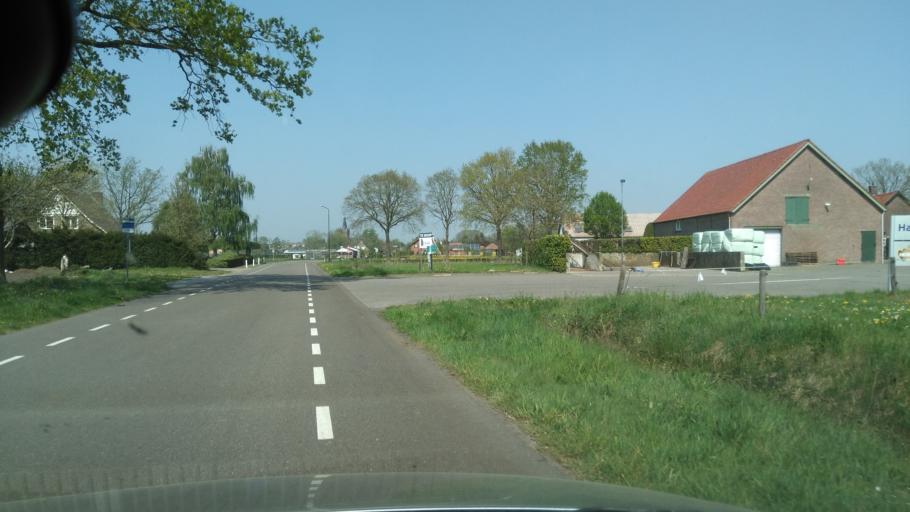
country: NL
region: North Brabant
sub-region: Gemeente Baarle-Nassau
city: Baarle-Nassau
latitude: 51.4976
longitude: 4.8604
